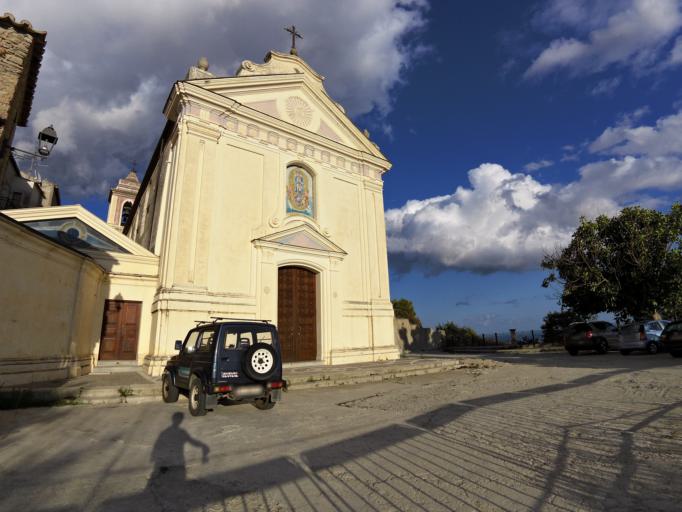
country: IT
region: Calabria
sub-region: Provincia di Reggio Calabria
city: Caulonia
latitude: 38.3792
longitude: 16.4087
